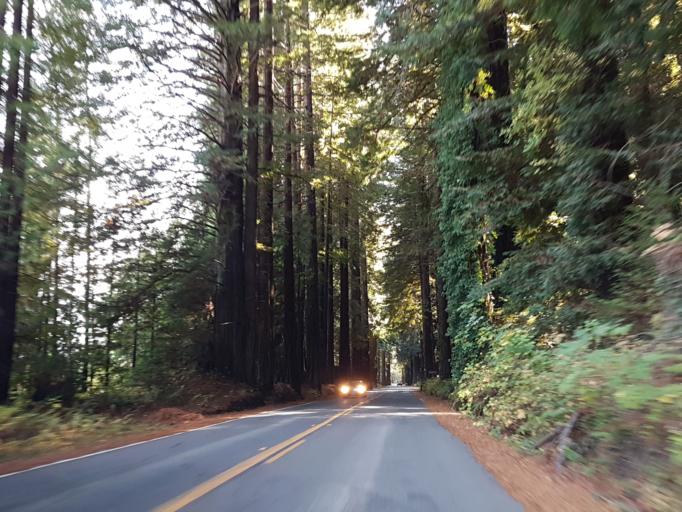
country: US
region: California
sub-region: Humboldt County
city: Rio Dell
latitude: 40.4380
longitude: -123.9853
